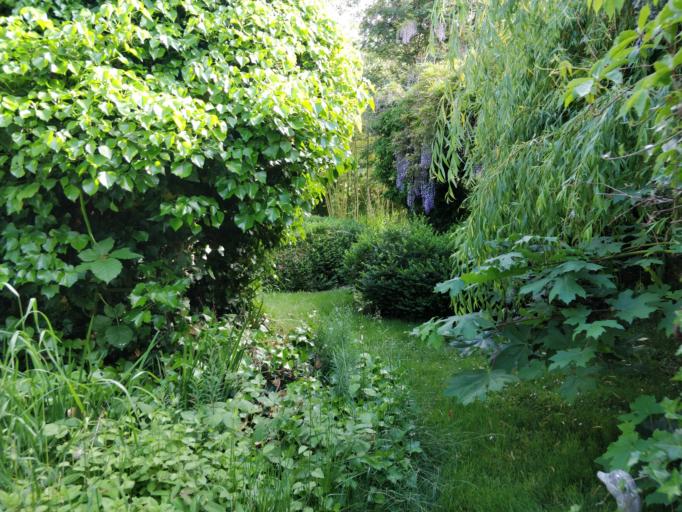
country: CA
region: British Columbia
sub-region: Cowichan Valley Regional District
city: Ladysmith
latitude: 49.0799
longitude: -123.8033
